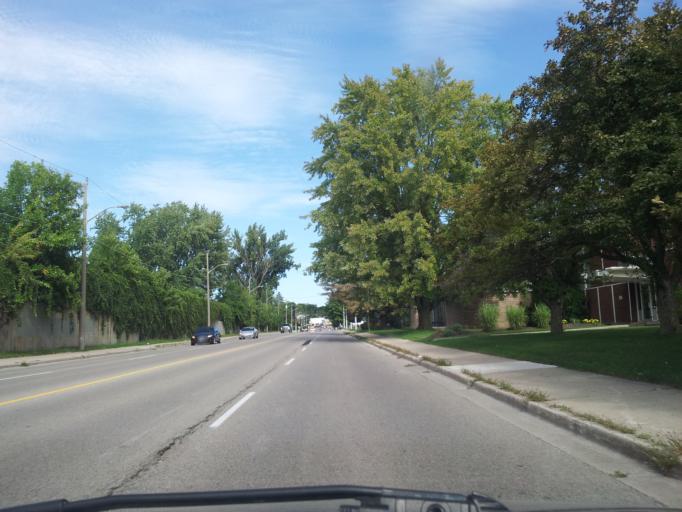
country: CA
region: Ontario
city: Kitchener
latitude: 43.4420
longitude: -80.4830
